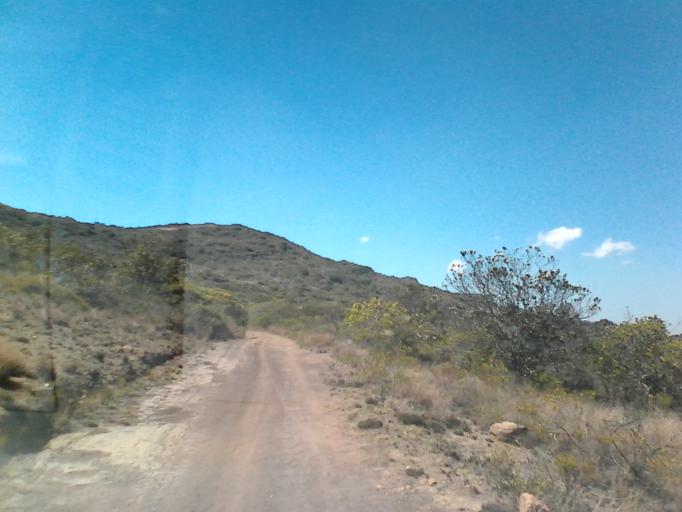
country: CO
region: Boyaca
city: Sachica
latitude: 5.5241
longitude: -73.5534
